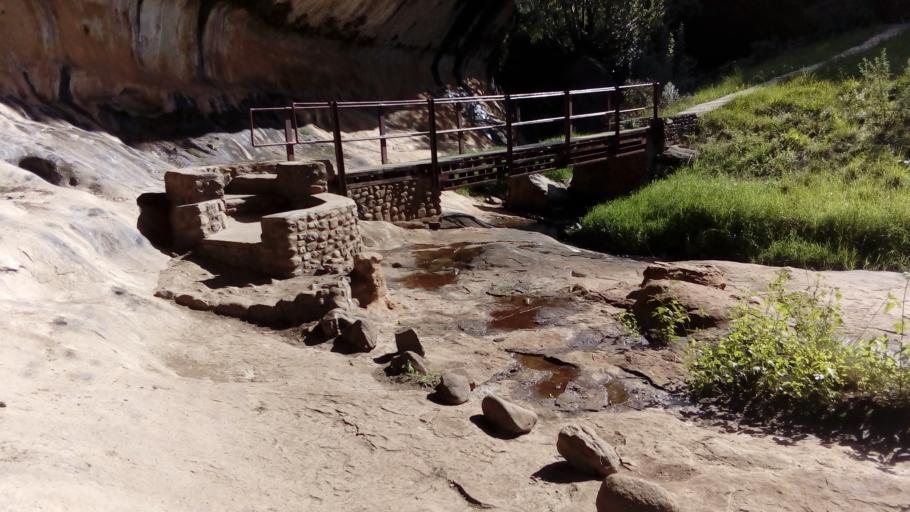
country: LS
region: Butha-Buthe
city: Butha-Buthe
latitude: -28.7539
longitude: 28.4947
